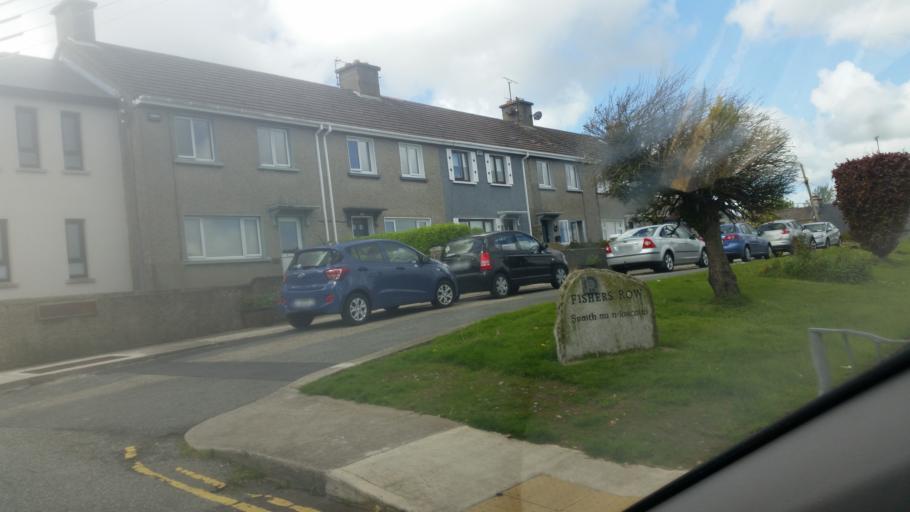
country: IE
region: Leinster
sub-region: Loch Garman
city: Loch Garman
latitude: 52.3324
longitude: -6.4534
